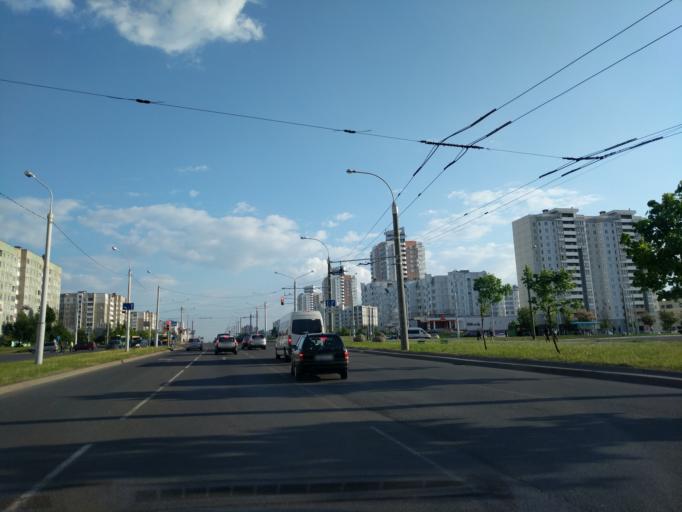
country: BY
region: Minsk
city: Zhdanovichy
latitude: 53.9171
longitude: 27.4369
